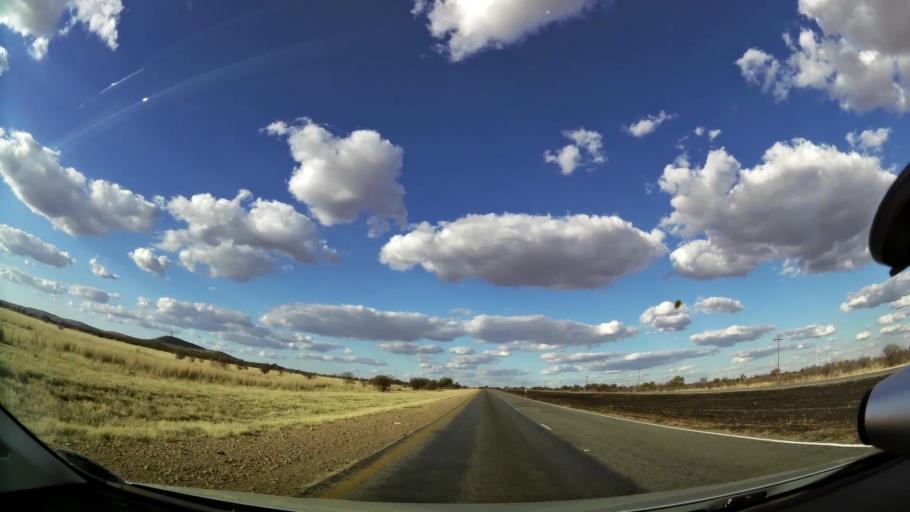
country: ZA
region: North-West
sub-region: Dr Kenneth Kaunda District Municipality
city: Stilfontein
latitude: -26.7873
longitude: 26.9323
